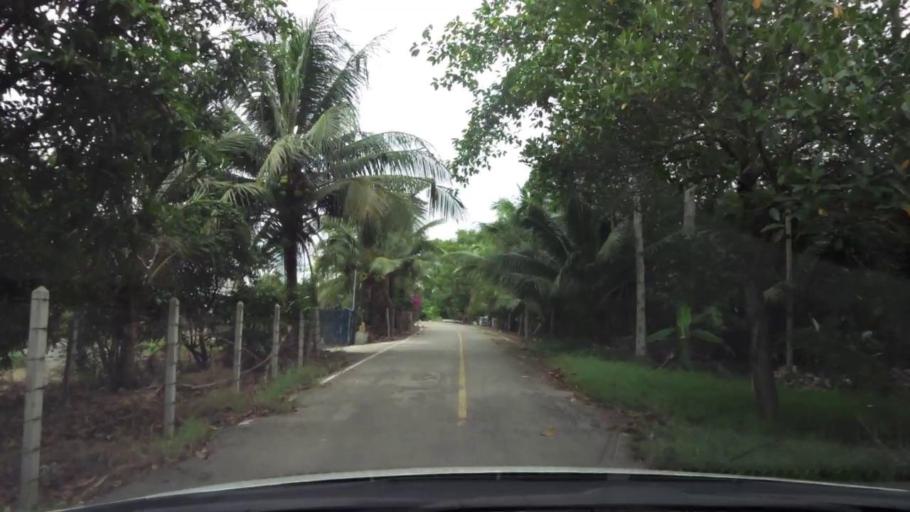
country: TH
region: Samut Sakhon
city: Ban Phaeo
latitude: 13.6061
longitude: 100.0276
